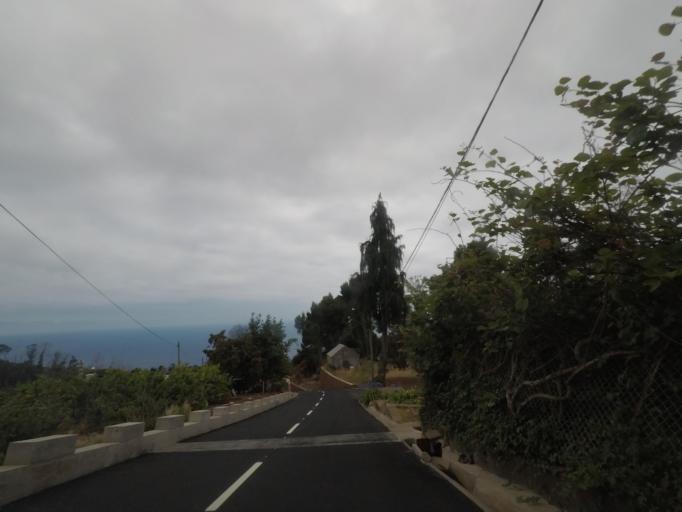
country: PT
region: Madeira
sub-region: Calheta
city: Estreito da Calheta
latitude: 32.7407
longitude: -17.1642
